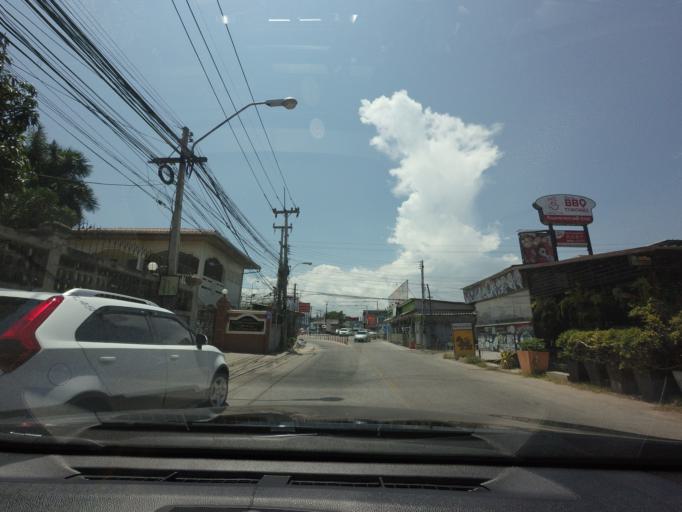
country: TH
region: Prachuap Khiri Khan
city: Hua Hin
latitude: 12.5613
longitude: 99.9564
